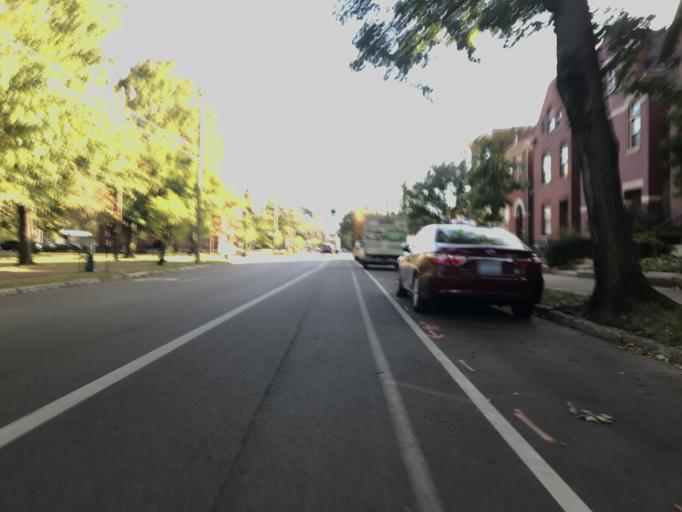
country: US
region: Kentucky
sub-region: Jefferson County
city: Louisville
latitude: 38.2405
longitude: -85.7628
